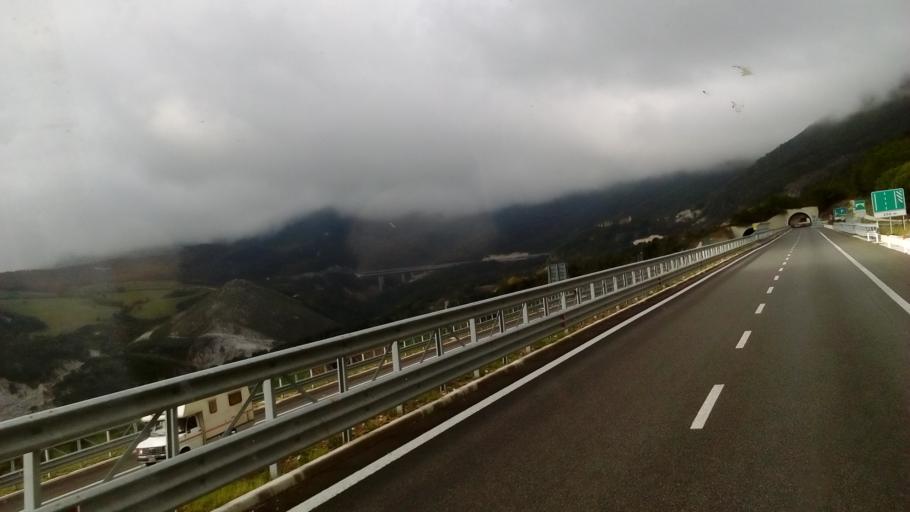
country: IT
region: Calabria
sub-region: Provincia di Cosenza
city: Morano Calabro
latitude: 39.8795
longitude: 16.1640
